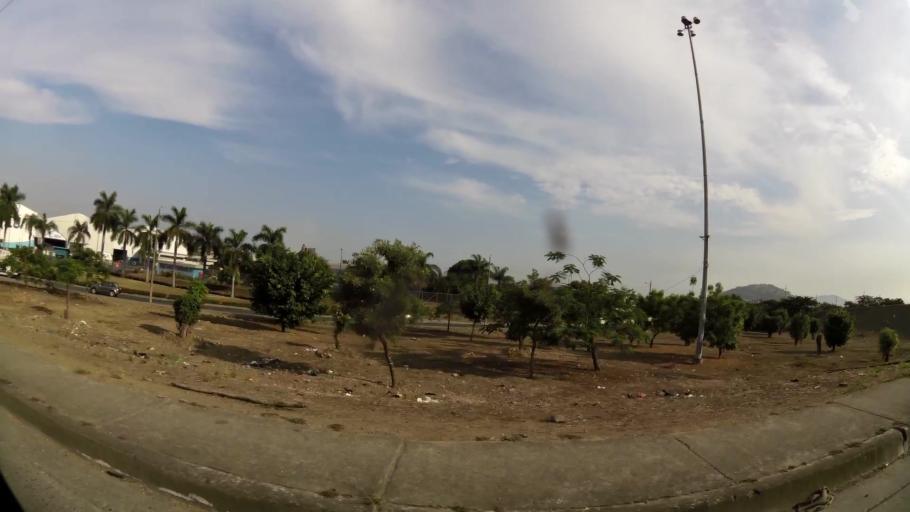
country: EC
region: Guayas
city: Eloy Alfaro
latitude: -2.0760
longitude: -79.9215
